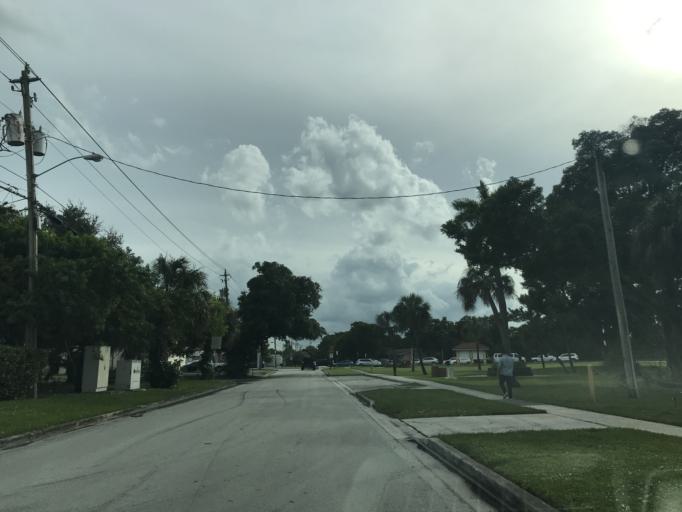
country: US
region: Florida
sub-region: Broward County
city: Margate
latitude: 26.2556
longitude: -80.2025
